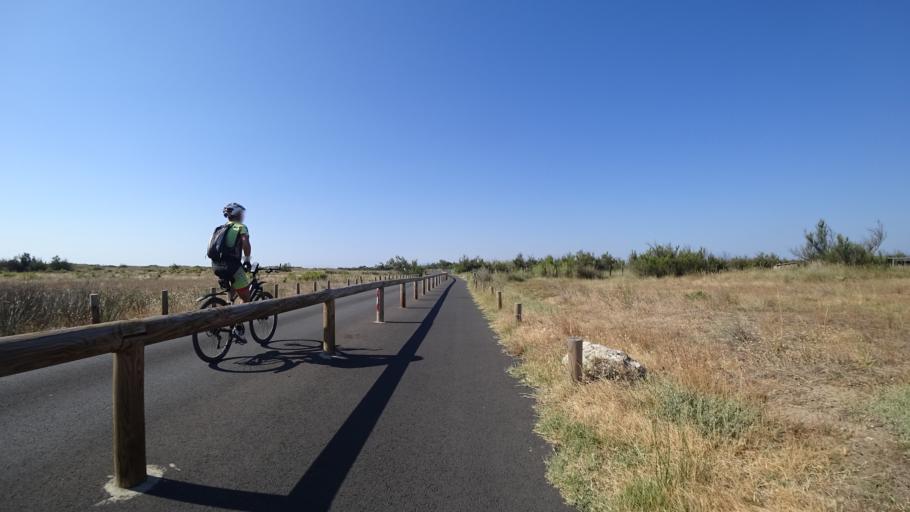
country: FR
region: Languedoc-Roussillon
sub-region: Departement de l'Aude
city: Leucate
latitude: 42.8972
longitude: 3.0518
